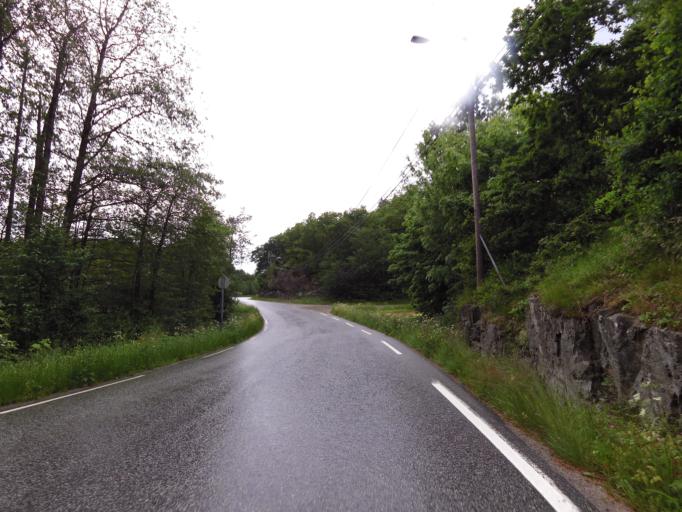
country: NO
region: Vest-Agder
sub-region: Mandal
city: Mandal
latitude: 58.0123
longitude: 7.5114
